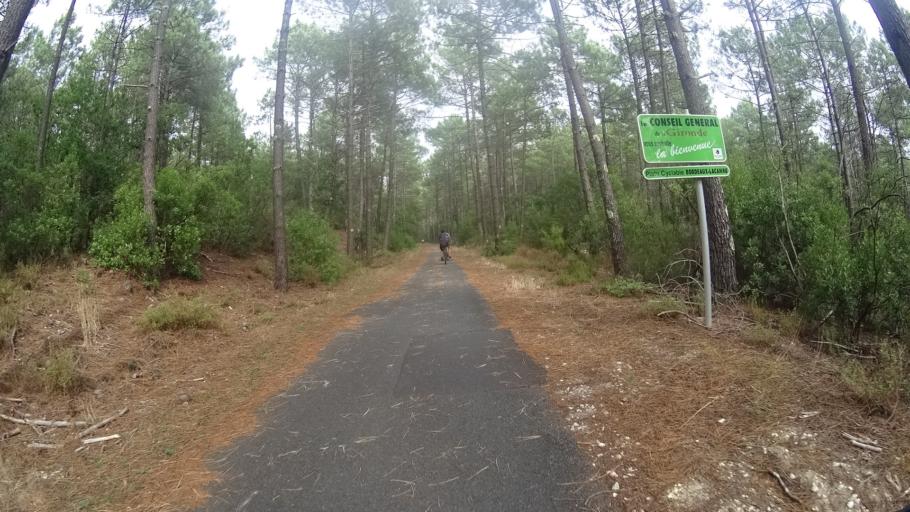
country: FR
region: Aquitaine
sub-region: Departement de la Gironde
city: Lacanau
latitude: 45.0074
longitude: -1.1503
